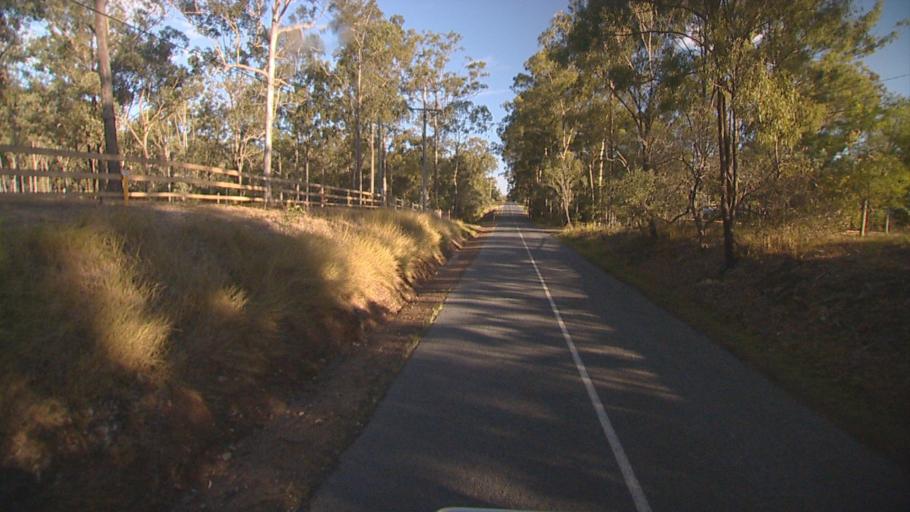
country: AU
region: Queensland
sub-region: Logan
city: Waterford West
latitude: -27.7294
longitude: 153.1465
